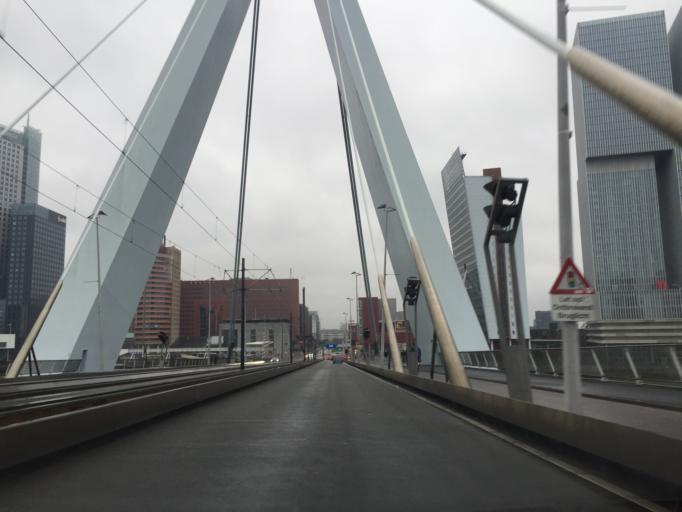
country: NL
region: South Holland
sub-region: Gemeente Rotterdam
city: Rotterdam
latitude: 51.9091
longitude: 4.4864
